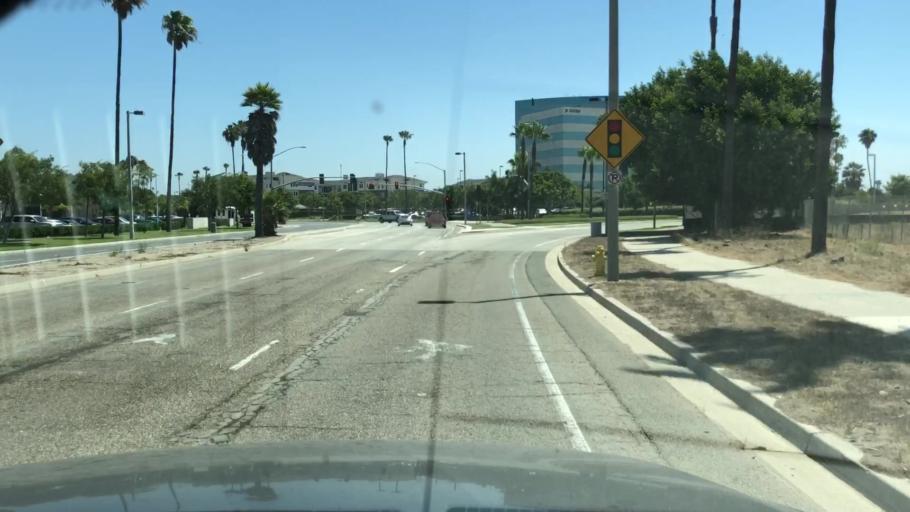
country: US
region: California
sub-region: Ventura County
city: El Rio
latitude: 34.2431
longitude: -119.1846
